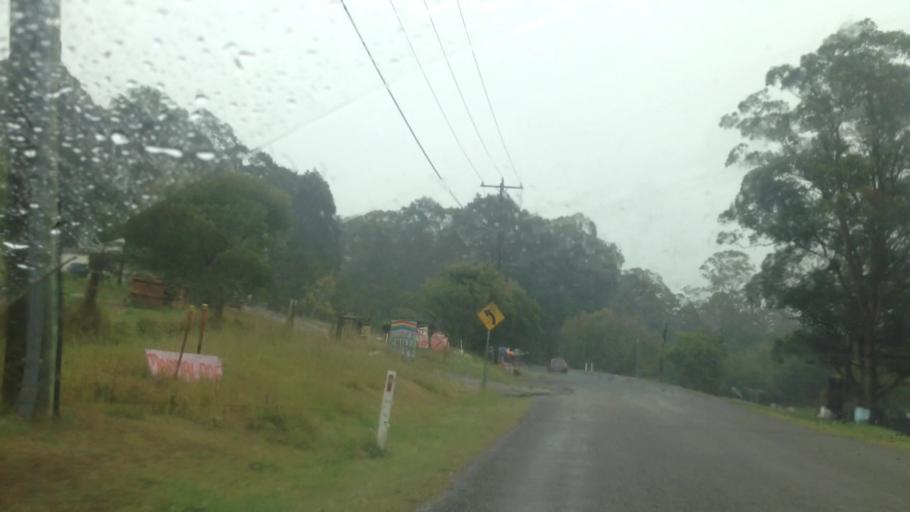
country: AU
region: New South Wales
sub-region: Wyong Shire
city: Little Jilliby
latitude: -33.2082
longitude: 151.3686
